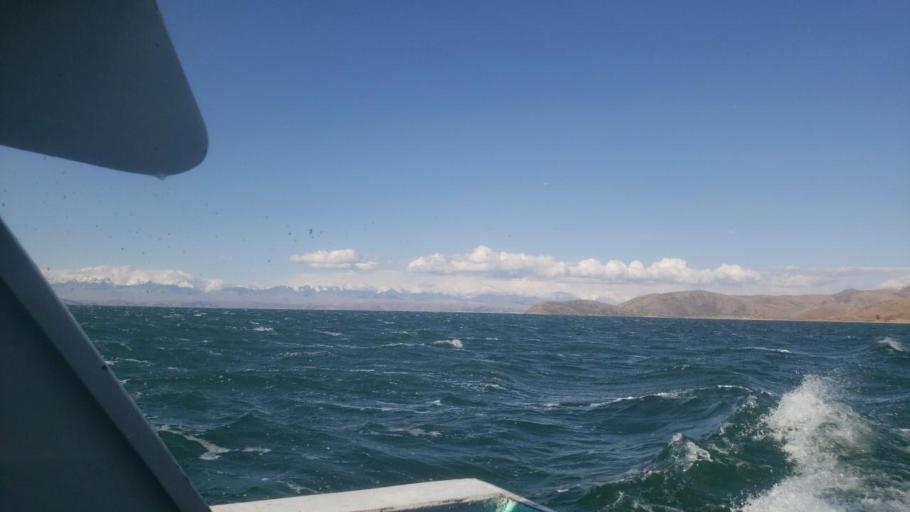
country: BO
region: La Paz
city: Huatajata
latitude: -16.3186
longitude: -68.7386
